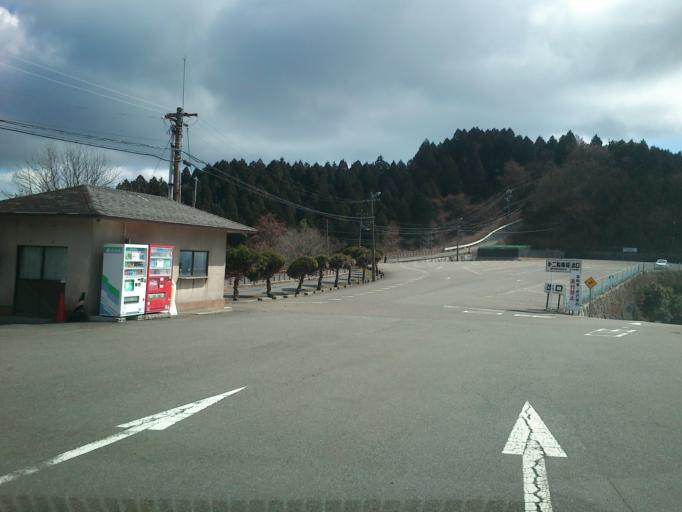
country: JP
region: Shiga Prefecture
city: Otsu-shi
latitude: 35.0659
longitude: 135.8316
